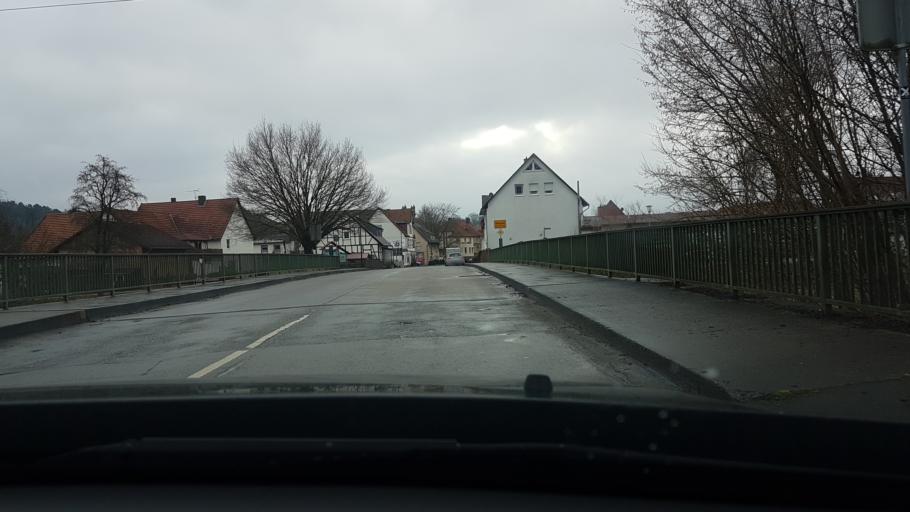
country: DE
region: North Rhine-Westphalia
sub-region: Regierungsbezirk Detmold
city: Willebadessen
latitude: 51.5124
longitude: 8.9966
